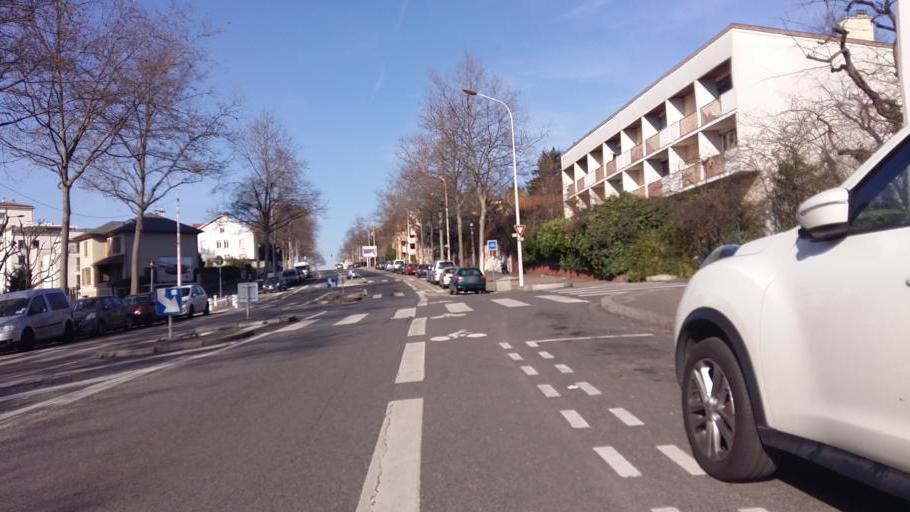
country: FR
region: Rhone-Alpes
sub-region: Departement du Rhone
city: Villeurbanne
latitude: 45.7382
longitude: 4.8846
